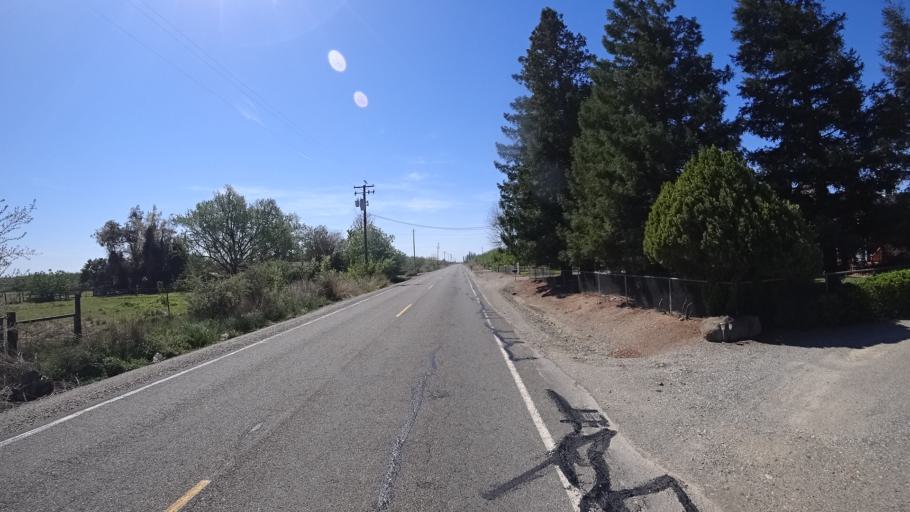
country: US
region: California
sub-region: Glenn County
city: Orland
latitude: 39.7405
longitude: -122.1410
